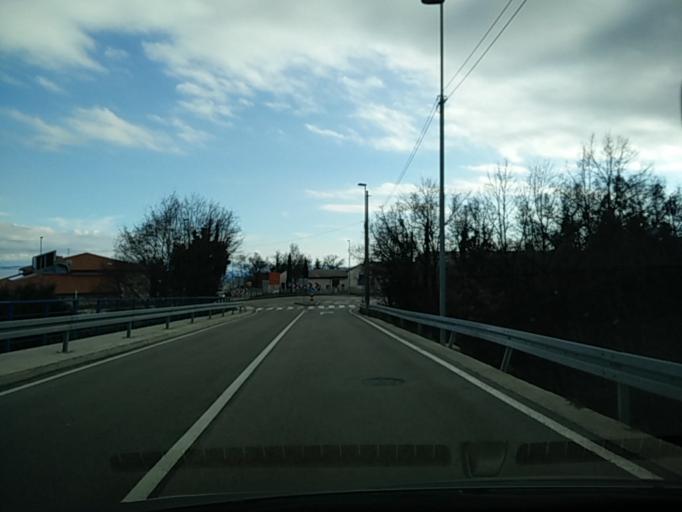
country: HR
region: Primorsko-Goranska
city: Matulji
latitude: 45.3648
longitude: 14.3125
